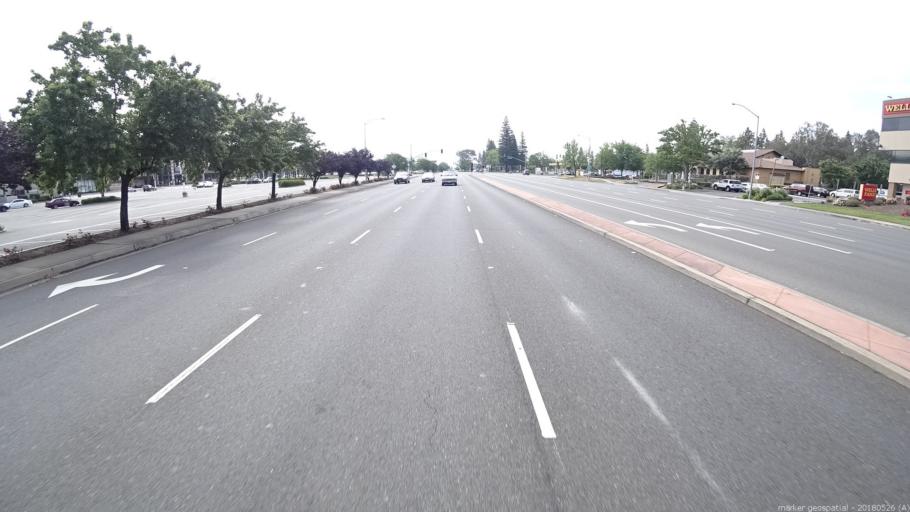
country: US
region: California
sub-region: Sacramento County
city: Arden-Arcade
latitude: 38.6010
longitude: -121.4298
